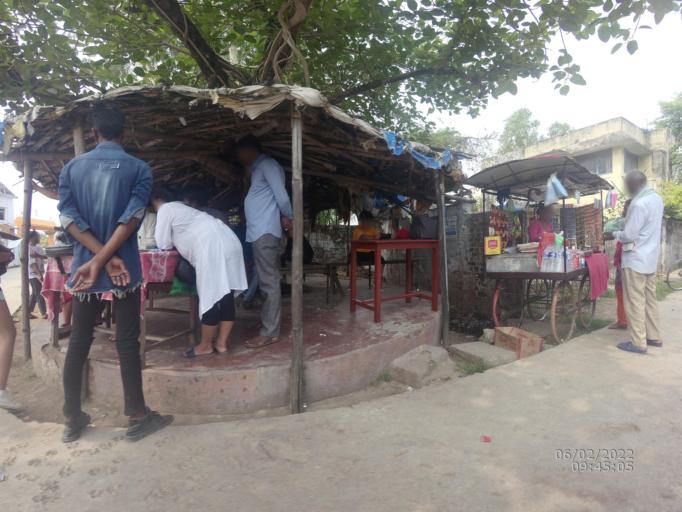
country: NP
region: Western Region
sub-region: Lumbini Zone
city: Bhairahawa
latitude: 27.5038
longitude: 83.4510
